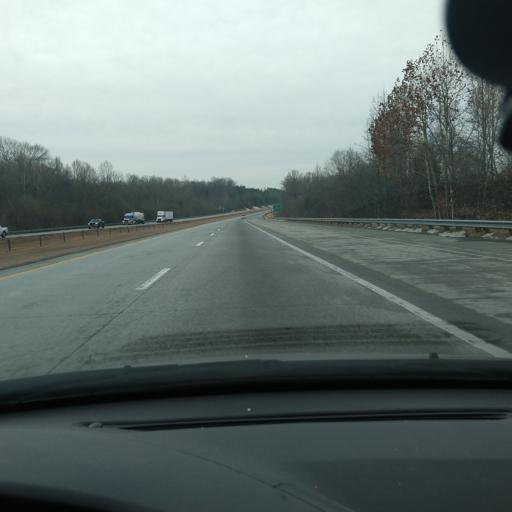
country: US
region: North Carolina
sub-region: Davidson County
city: Lexington
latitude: 35.8564
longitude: -80.2725
